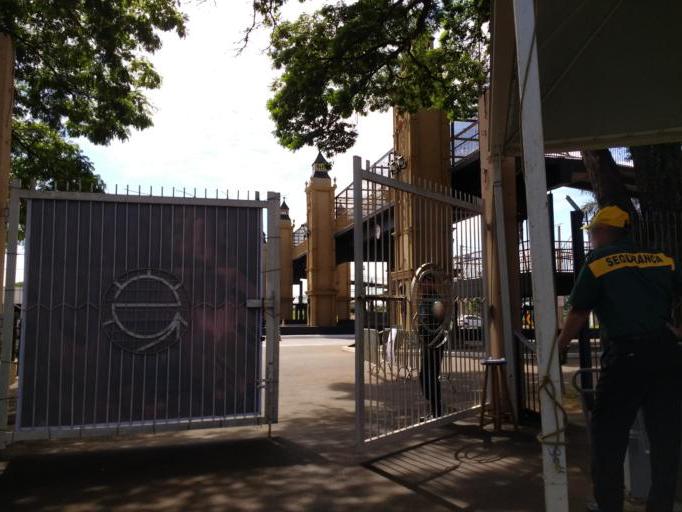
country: BR
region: Parana
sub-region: Cambe
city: Cambe
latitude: -23.2884
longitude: -51.2257
